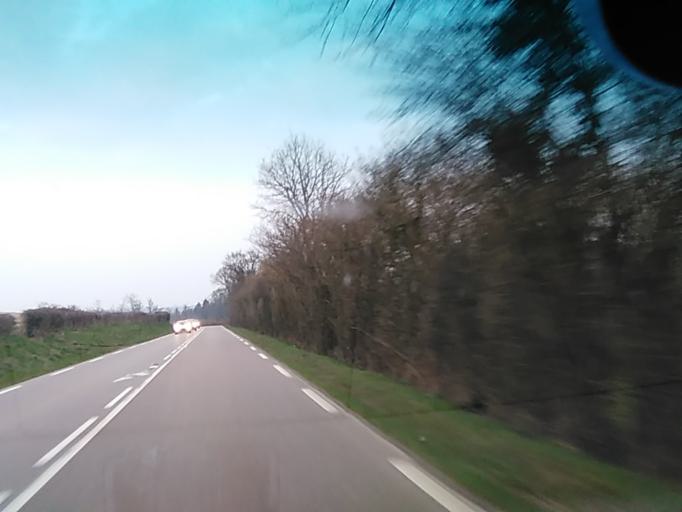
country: FR
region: Lower Normandy
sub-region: Departement de l'Orne
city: Pont-Ecrepin
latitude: 48.7399
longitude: -0.2459
